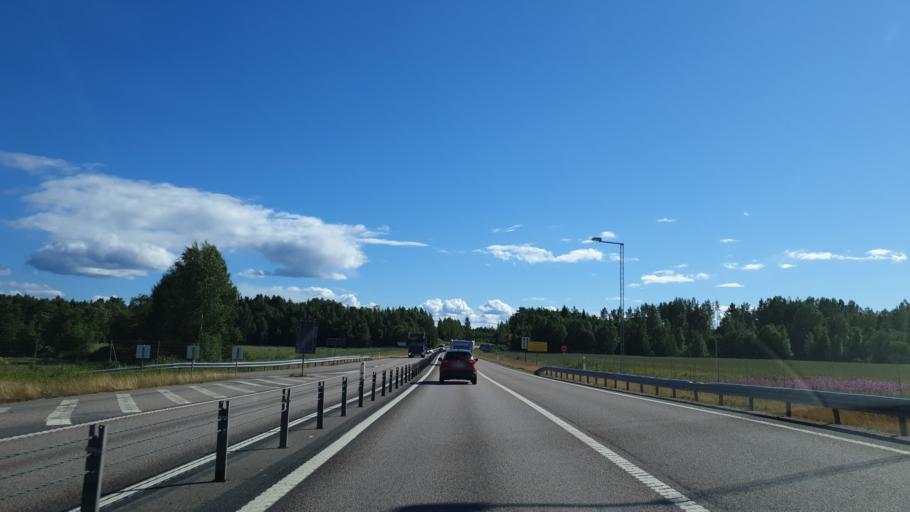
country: SE
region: Gaevleborg
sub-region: Hudiksvalls Kommun
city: Hudiksvall
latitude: 61.7643
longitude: 17.0948
